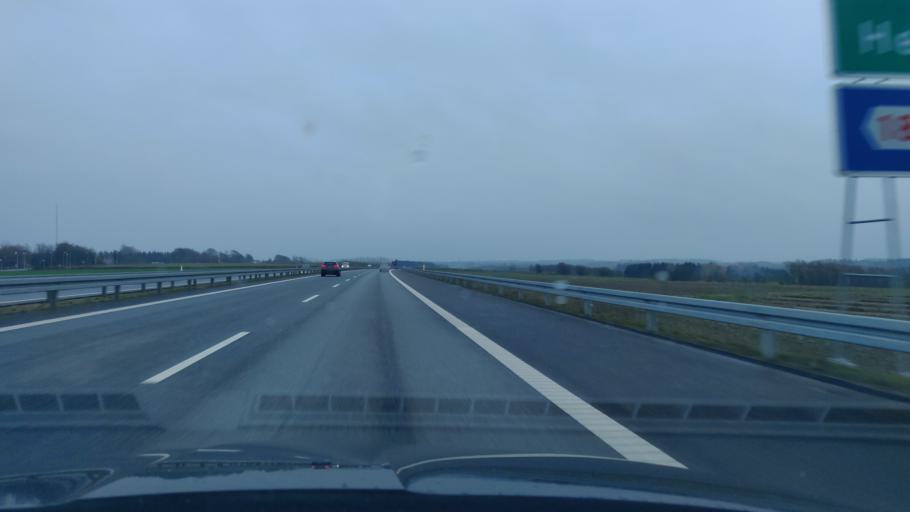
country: DK
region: Central Jutland
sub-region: Herning Kommune
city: Avlum
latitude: 56.2498
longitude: 8.7919
